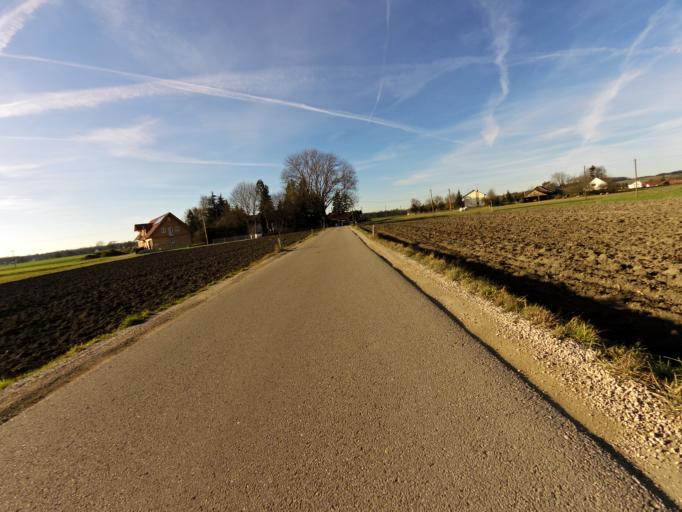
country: DE
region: Bavaria
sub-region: Upper Bavaria
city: Wang
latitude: 48.4896
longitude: 11.9724
